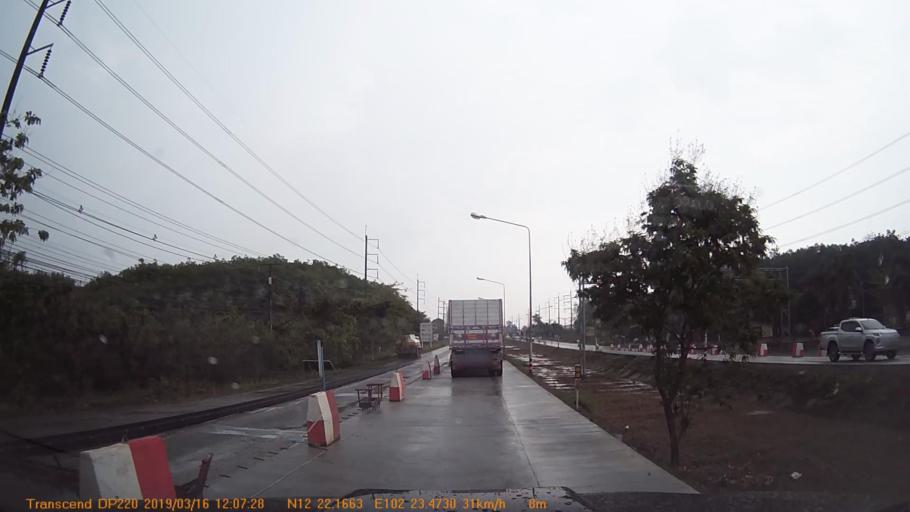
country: TH
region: Trat
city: Khao Saming
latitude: 12.3663
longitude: 102.3997
